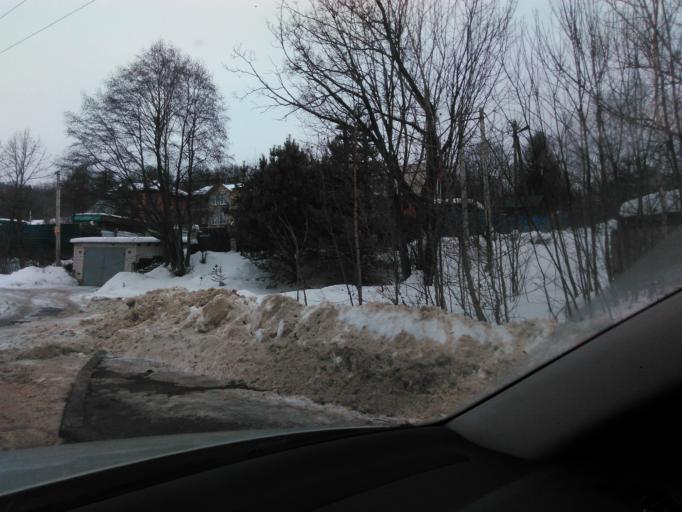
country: RU
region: Moskovskaya
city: Yakhroma
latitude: 56.2950
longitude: 37.4976
